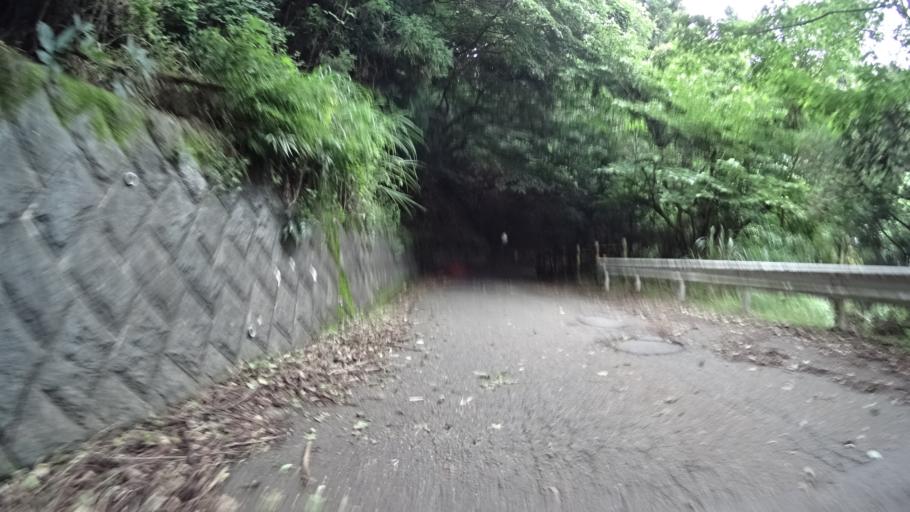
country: JP
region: Kanagawa
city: Atsugi
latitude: 35.5013
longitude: 139.2747
